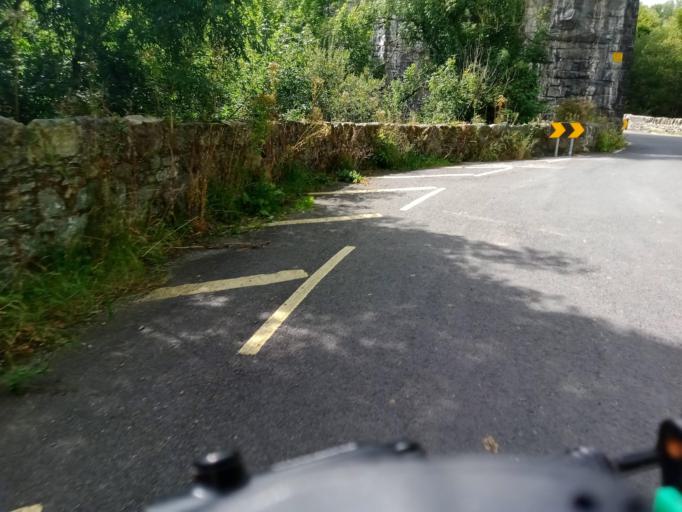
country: IE
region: Munster
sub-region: Waterford
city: Dungarvan
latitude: 52.1401
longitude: -7.5041
